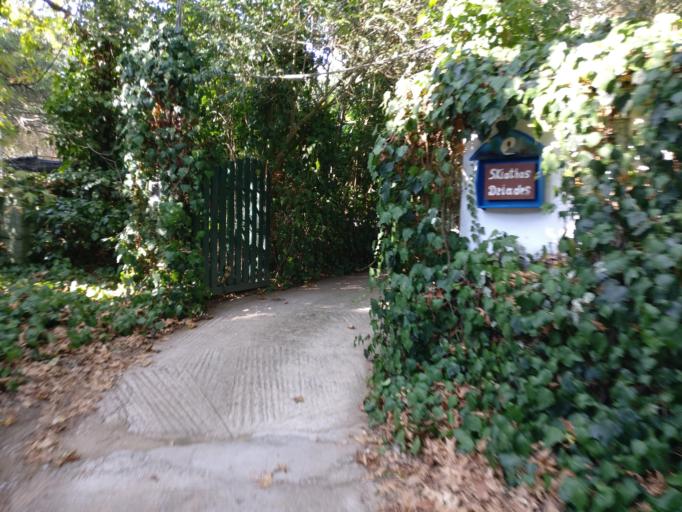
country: GR
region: Thessaly
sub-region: Nomos Magnisias
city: Skiathos
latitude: 39.1525
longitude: 23.4093
